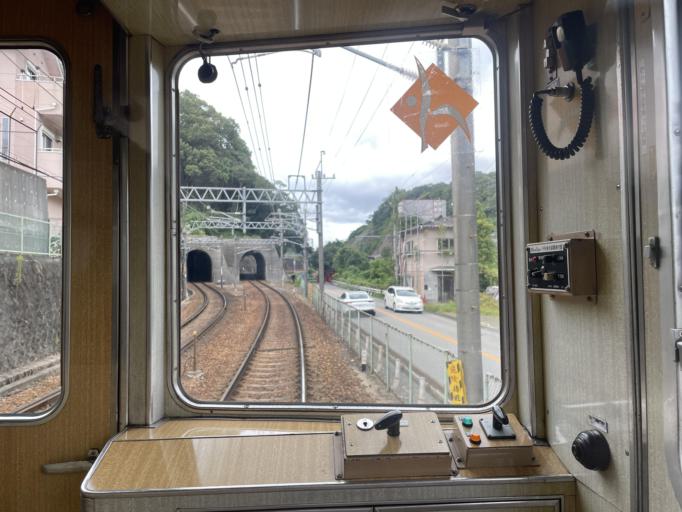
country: JP
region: Osaka
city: Ikeda
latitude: 34.8488
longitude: 135.4185
